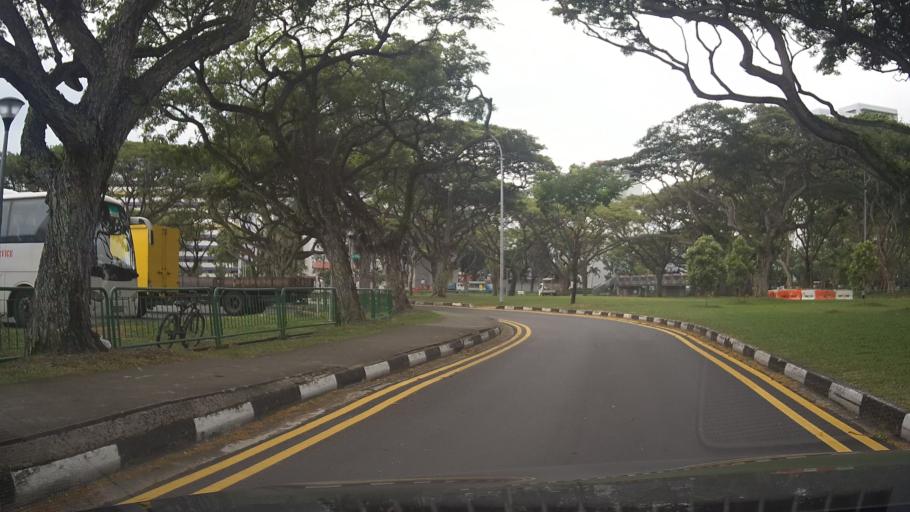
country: SG
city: Singapore
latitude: 1.3039
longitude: 103.8814
